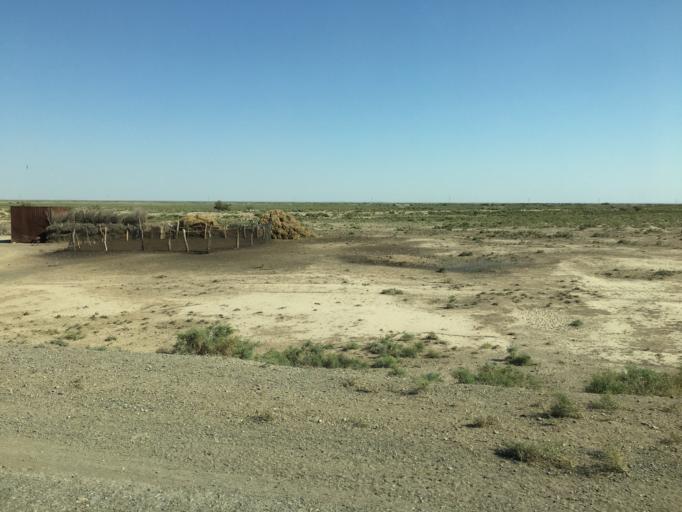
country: IR
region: Razavi Khorasan
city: Sarakhs
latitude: 36.5912
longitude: 61.2862
